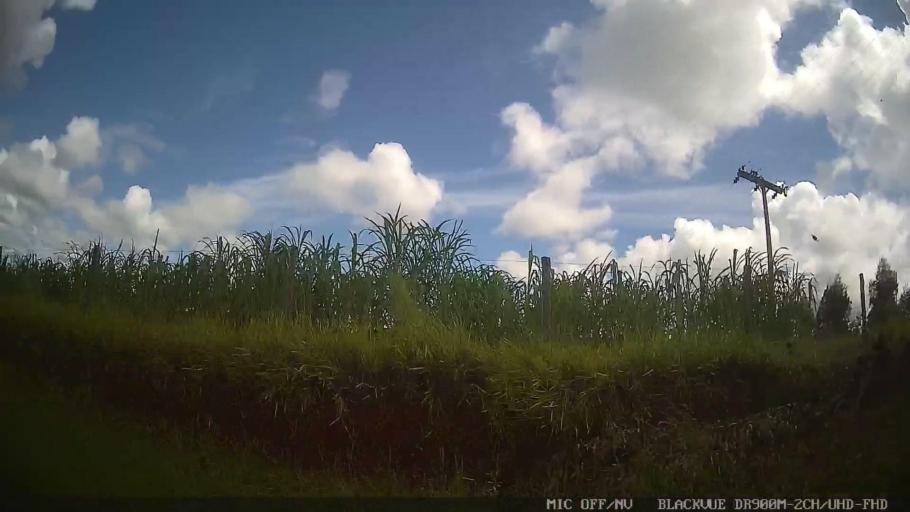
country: BR
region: Sao Paulo
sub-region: Braganca Paulista
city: Braganca Paulista
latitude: -22.8629
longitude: -46.6405
